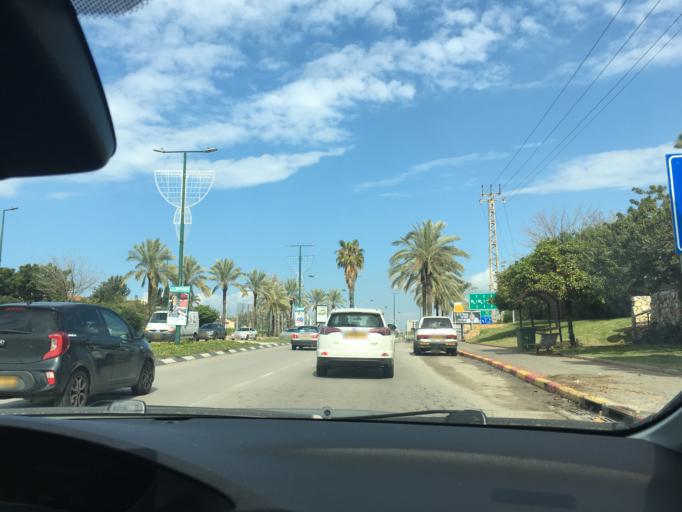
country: IL
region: Central District
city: Ra'anana
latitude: 32.1762
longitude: 34.8515
